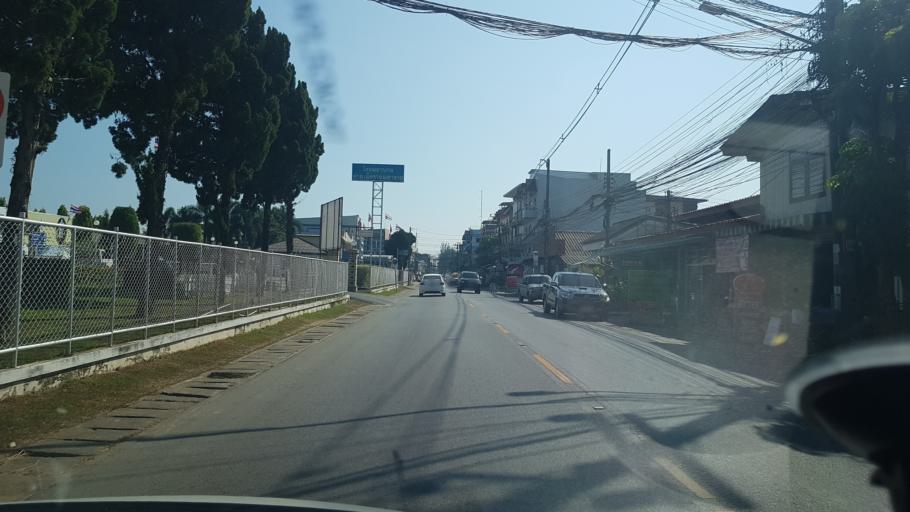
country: TH
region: Chiang Rai
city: Chiang Rai
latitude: 19.9040
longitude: 99.8126
